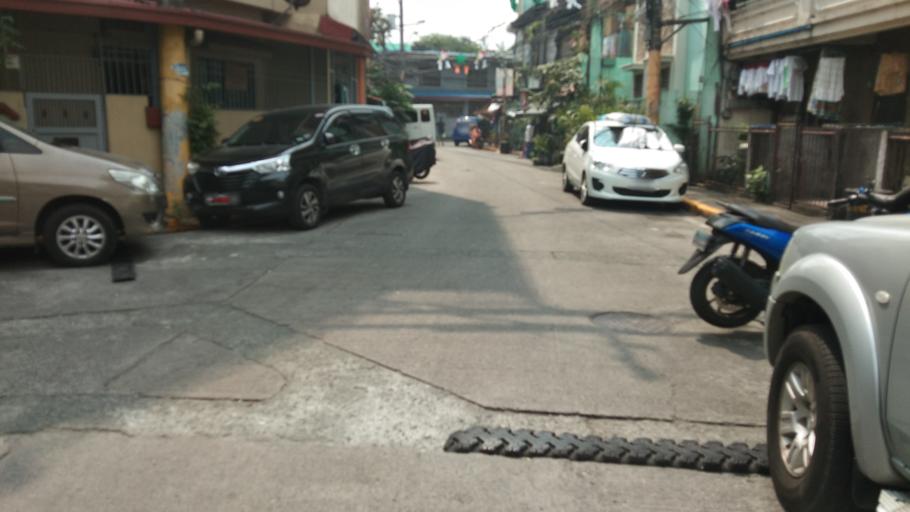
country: PH
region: Metro Manila
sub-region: City of Manila
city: Quiapo
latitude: 14.5769
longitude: 120.9991
